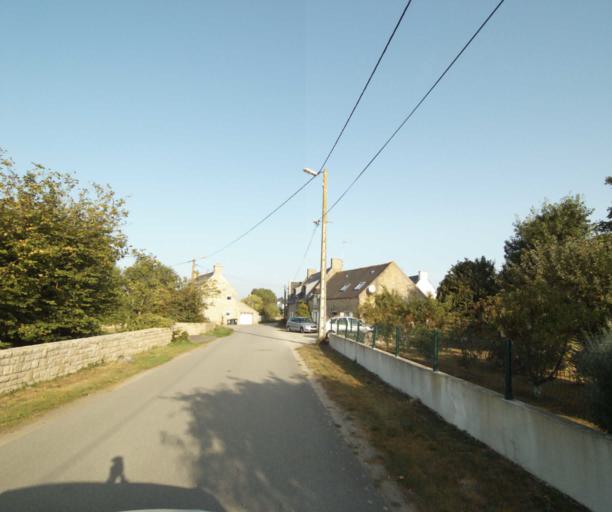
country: FR
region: Brittany
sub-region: Departement du Morbihan
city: Riantec
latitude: 47.7045
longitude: -3.2982
